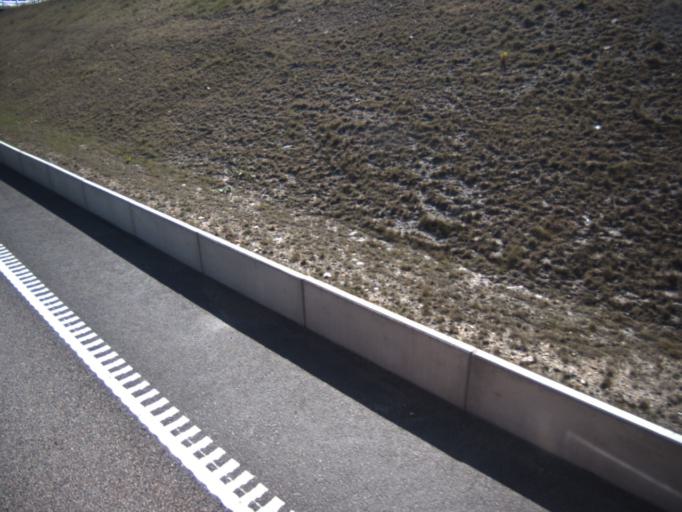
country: SE
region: Skane
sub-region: Helsingborg
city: Gantofta
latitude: 56.0288
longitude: 12.7614
